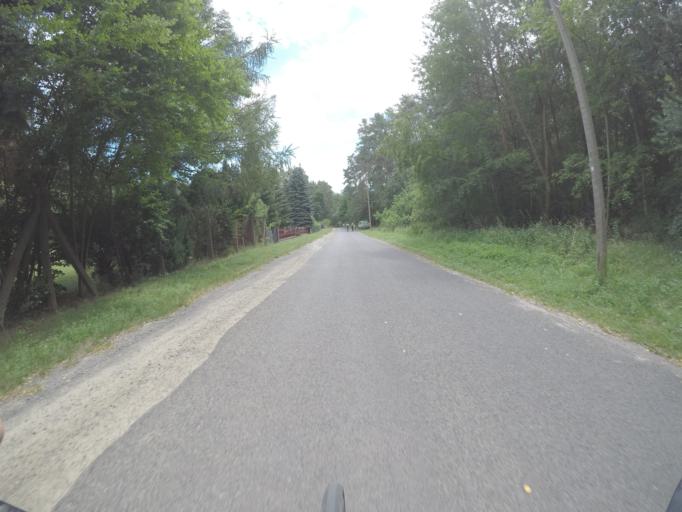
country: DE
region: Brandenburg
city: Storkow
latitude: 52.2445
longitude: 13.9561
